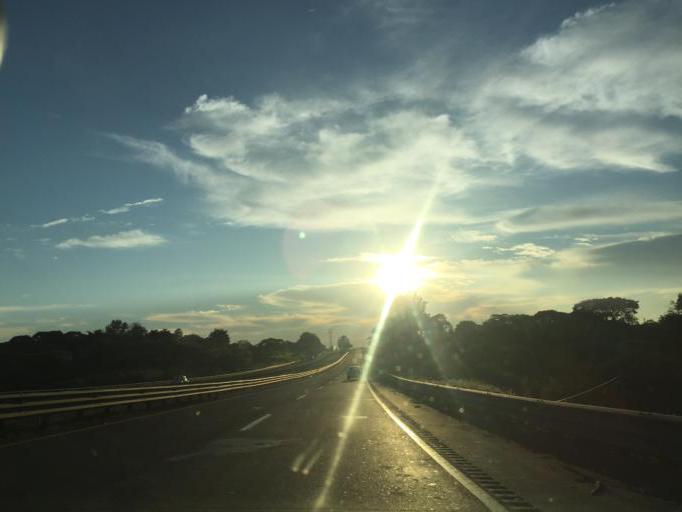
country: MX
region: Veracruz
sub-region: Fortin
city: Fortin de las Flores
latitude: 18.9075
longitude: -96.9938
